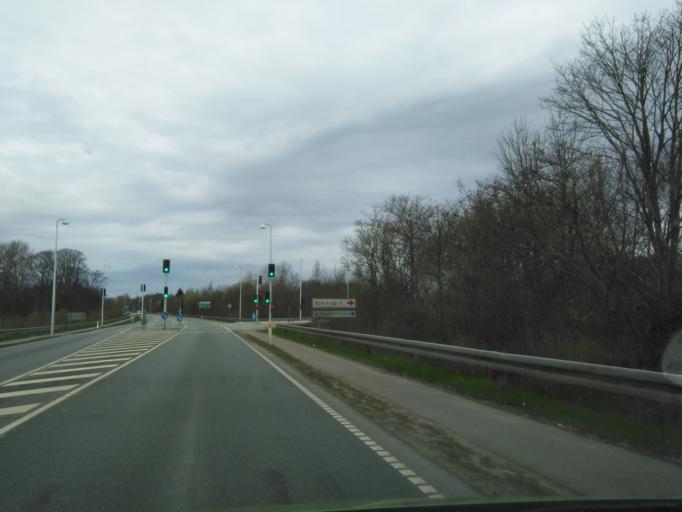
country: DK
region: Central Jutland
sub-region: Skanderborg Kommune
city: Stilling
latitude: 56.0628
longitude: 9.9788
